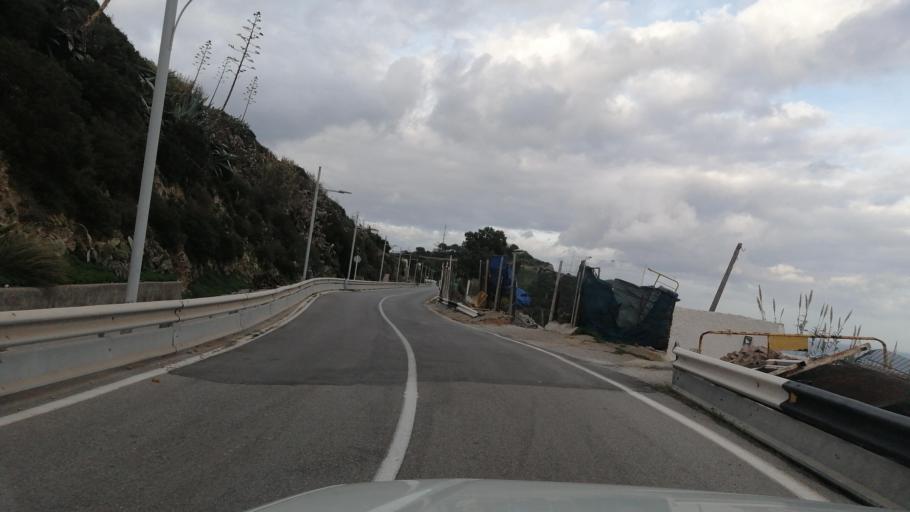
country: ES
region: Ceuta
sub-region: Ceuta
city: Ceuta
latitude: 35.8927
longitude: -5.2871
